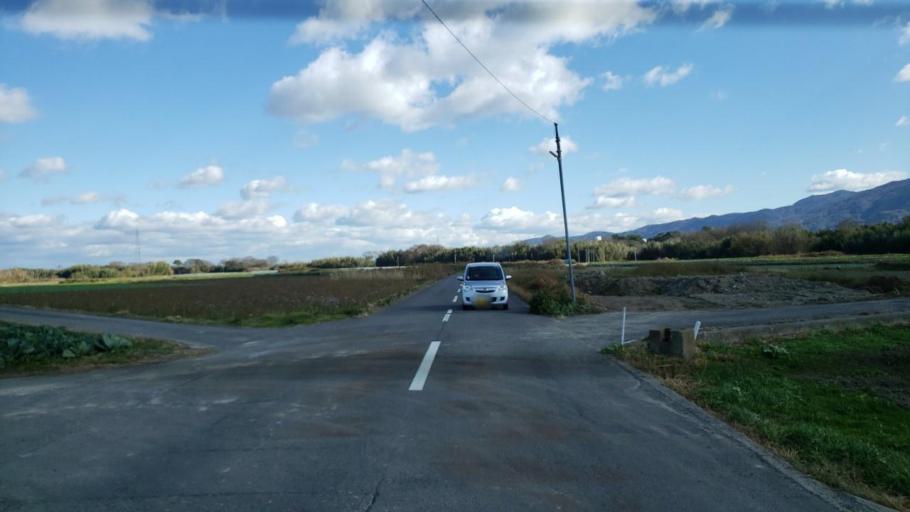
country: JP
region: Tokushima
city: Kamojimacho-jogejima
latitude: 34.0700
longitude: 134.3089
